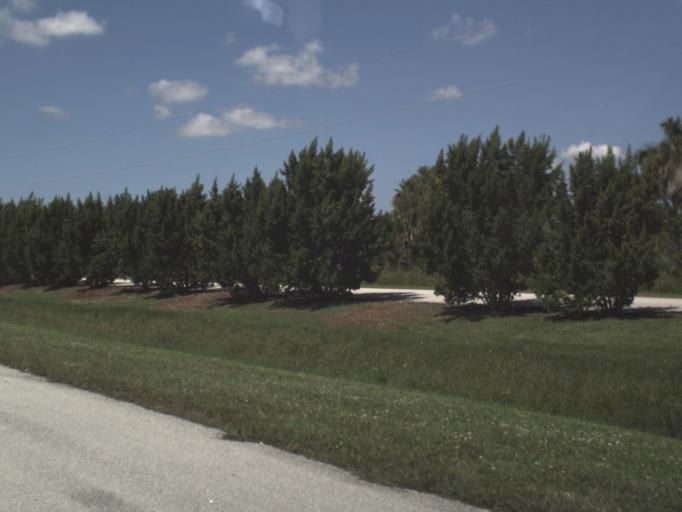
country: US
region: Florida
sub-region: Lee County
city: Lochmoor Waterway Estates
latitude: 26.6078
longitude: -81.9257
